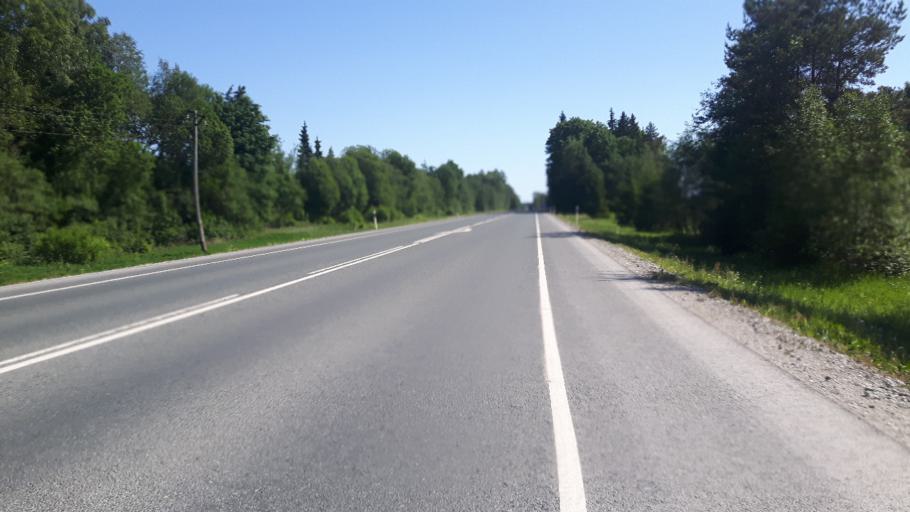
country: EE
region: Raplamaa
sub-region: Rapla vald
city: Rapla
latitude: 59.0481
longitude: 24.8377
